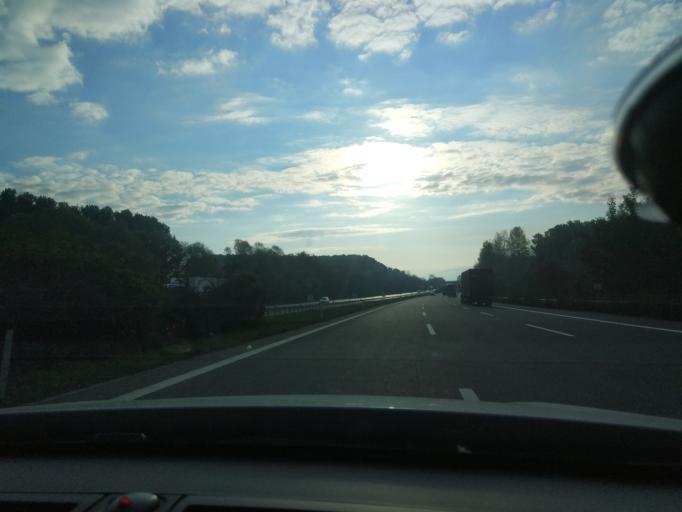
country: TR
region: Duzce
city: Duzce
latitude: 40.8101
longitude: 31.1412
